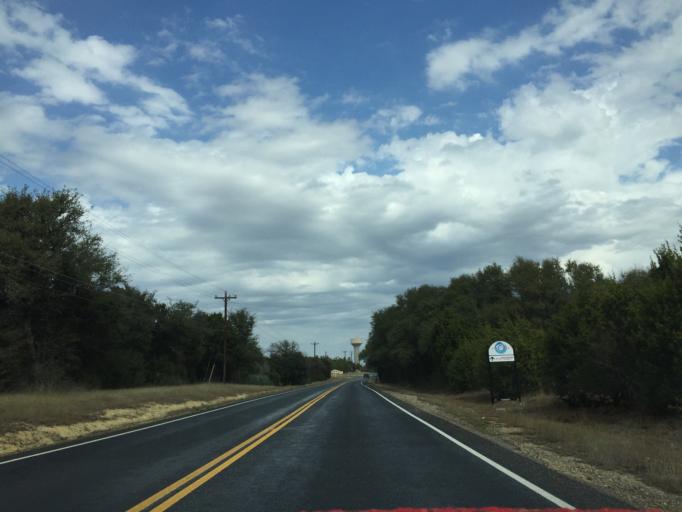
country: US
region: Texas
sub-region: Burnet County
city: Bertram
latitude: 30.6913
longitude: -97.9356
